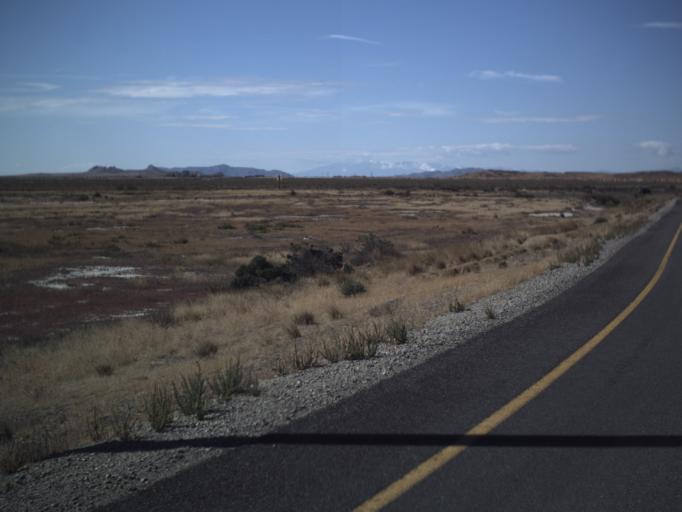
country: US
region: Utah
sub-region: Tooele County
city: Grantsville
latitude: 40.7332
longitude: -113.1158
